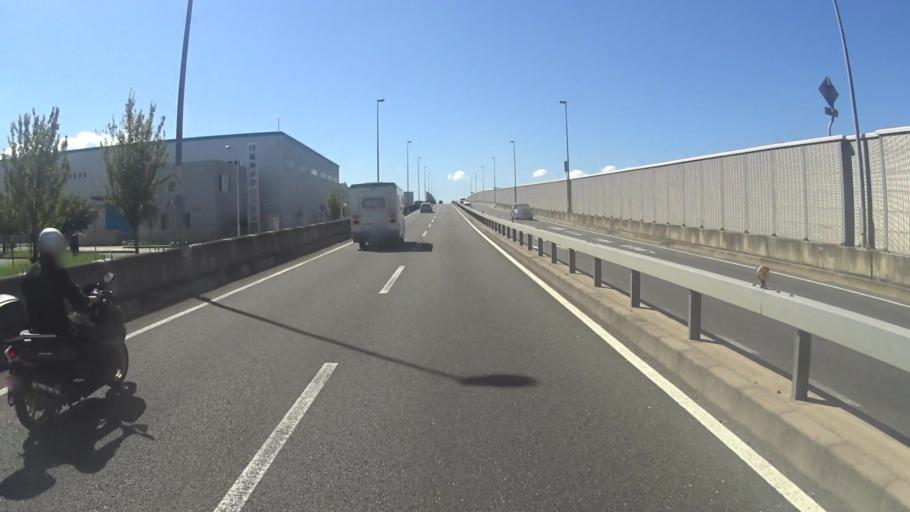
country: JP
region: Kyoto
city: Uji
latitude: 34.8775
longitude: 135.7623
